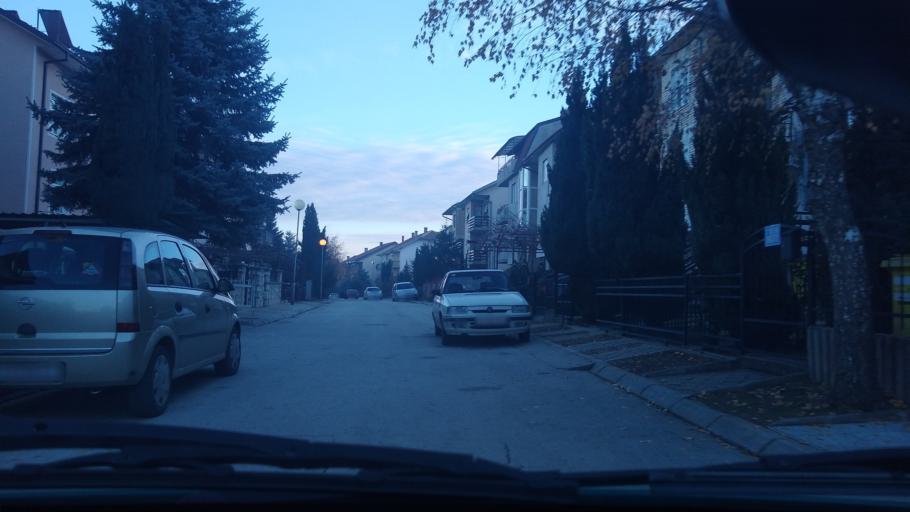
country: MK
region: Bitola
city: Bitola
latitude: 41.0254
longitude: 21.3051
